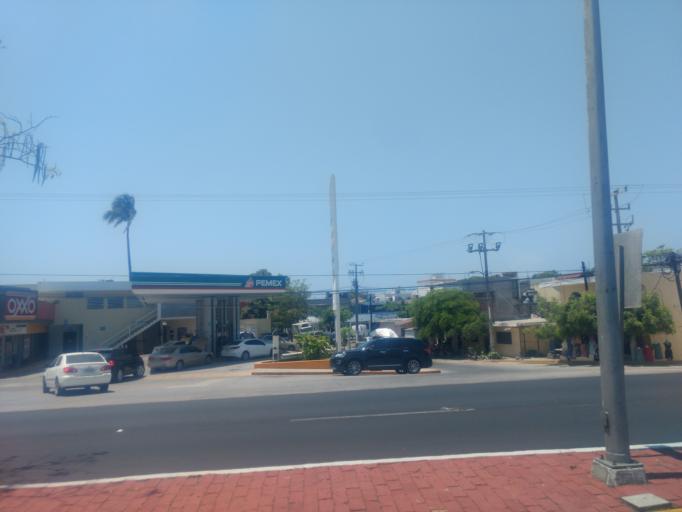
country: MX
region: Colima
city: Tapeixtles
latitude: 19.0854
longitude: -104.3069
